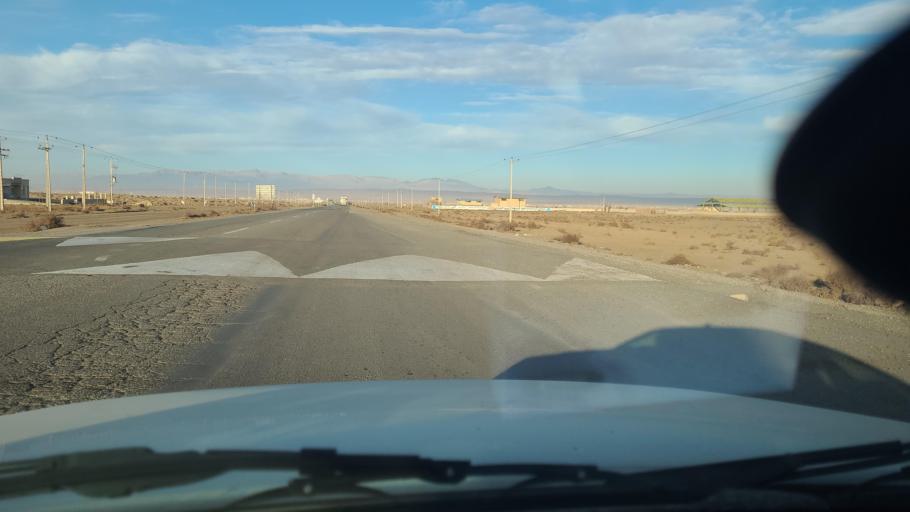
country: IR
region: Razavi Khorasan
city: Neqab
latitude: 36.5872
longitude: 57.5830
